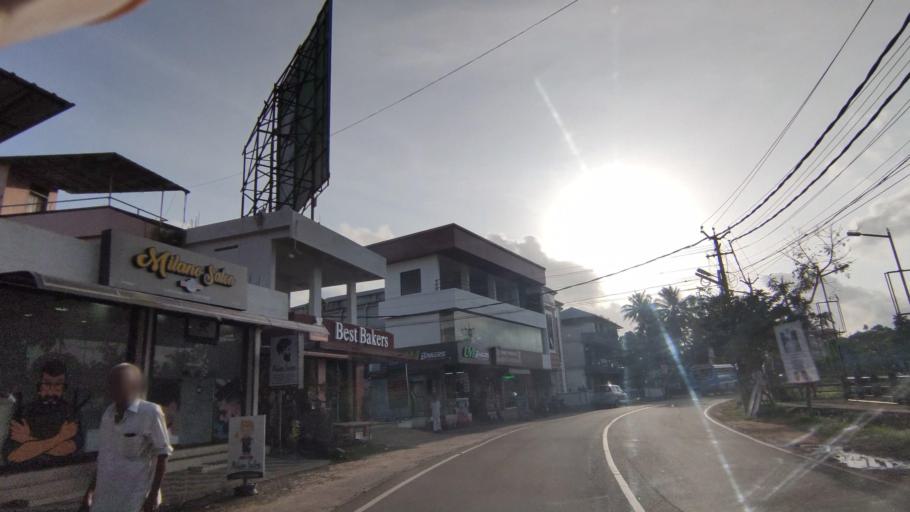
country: IN
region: Kerala
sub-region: Kottayam
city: Kottayam
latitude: 9.5903
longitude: 76.4985
